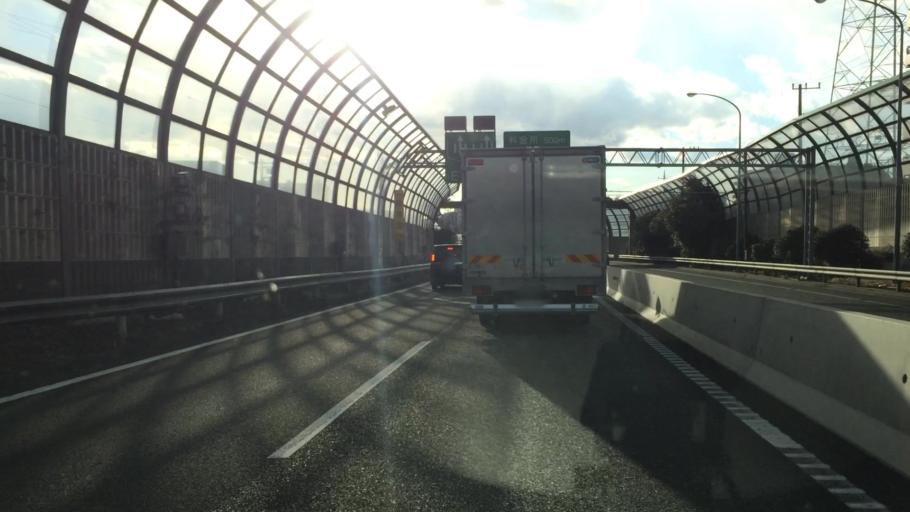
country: JP
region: Kanagawa
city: Yokohama
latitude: 35.4266
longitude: 139.5431
